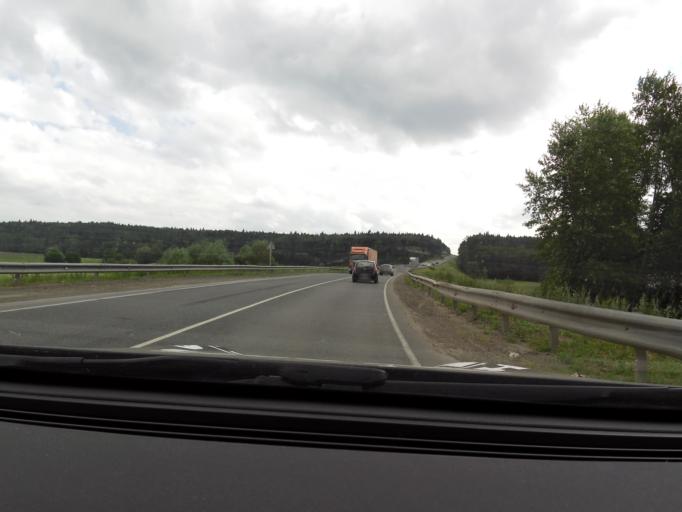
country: RU
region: Perm
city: Kungur
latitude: 57.4512
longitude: 56.8070
